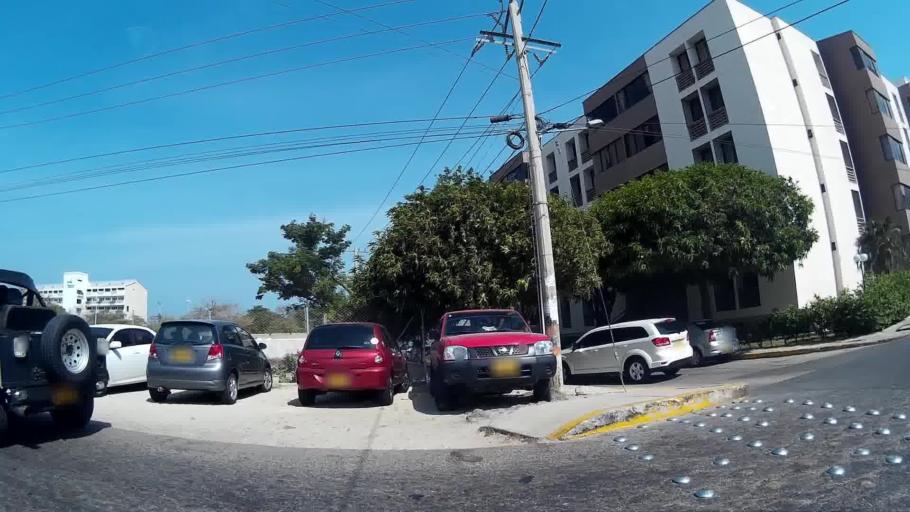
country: CO
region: Magdalena
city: Santa Marta
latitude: 11.2015
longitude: -74.2259
